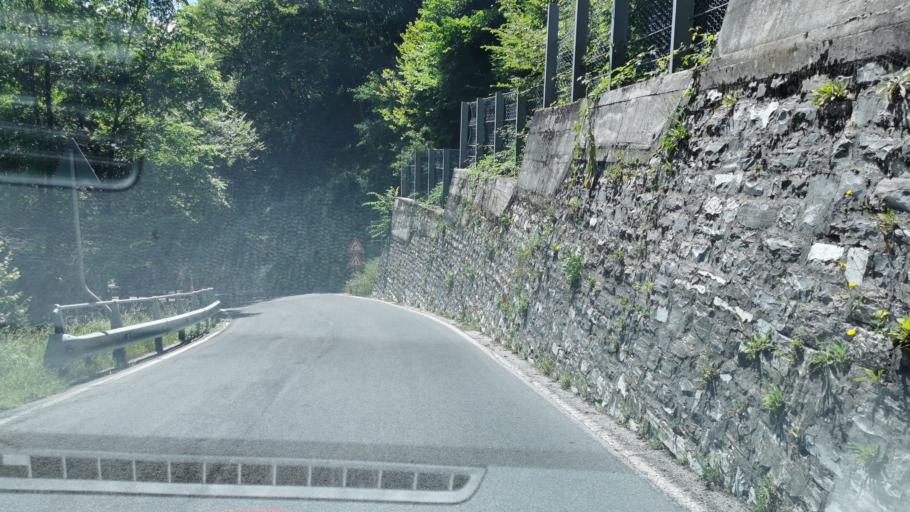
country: IT
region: Lombardy
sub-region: Provincia di Como
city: Lanzo d'Intelvi
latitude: 45.9629
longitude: 9.0098
